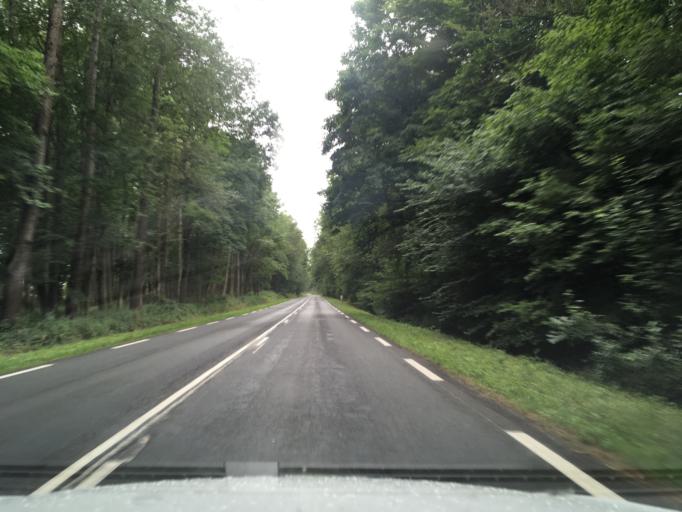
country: FR
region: Picardie
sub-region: Departement de l'Aisne
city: Esqueheries
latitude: 49.9420
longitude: 3.7589
